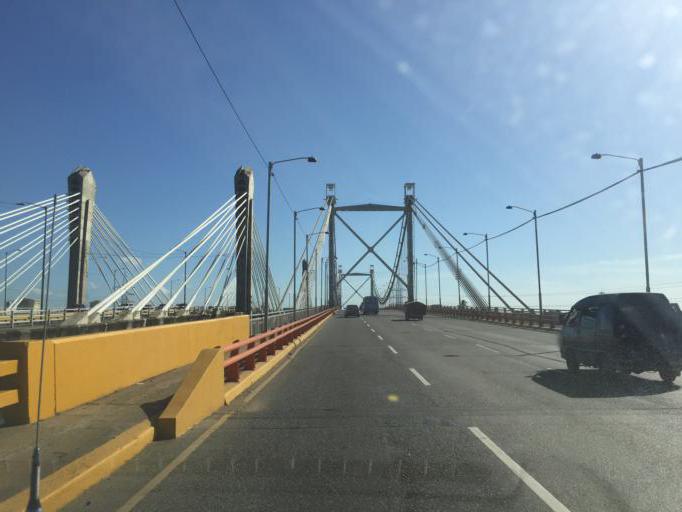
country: DO
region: Nacional
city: San Carlos
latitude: 18.4865
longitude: -69.8847
